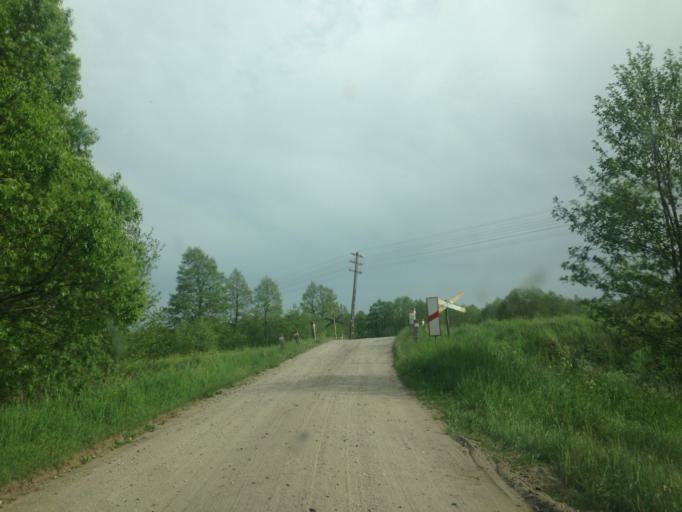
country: PL
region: Kujawsko-Pomorskie
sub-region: Powiat brodnicki
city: Brodnica
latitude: 53.2771
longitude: 19.4880
